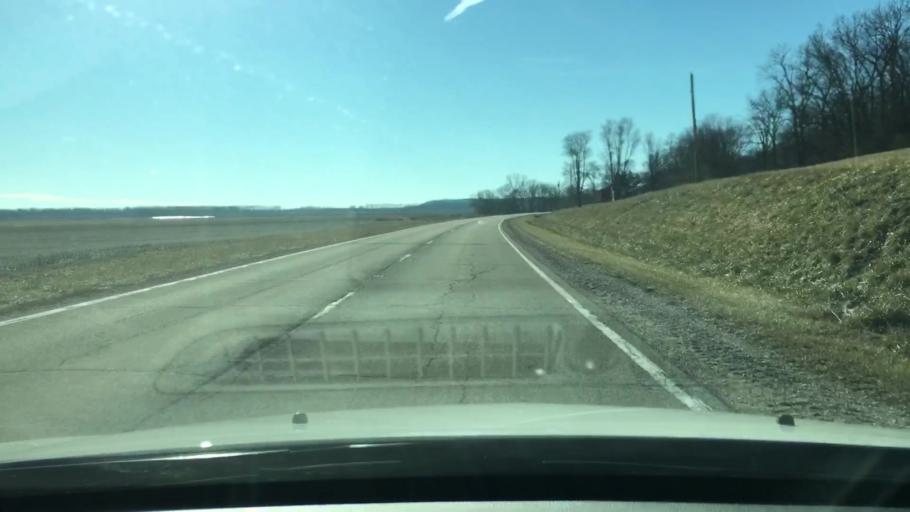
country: US
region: Illinois
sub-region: Mason County
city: Havana
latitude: 40.2571
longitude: -90.1792
